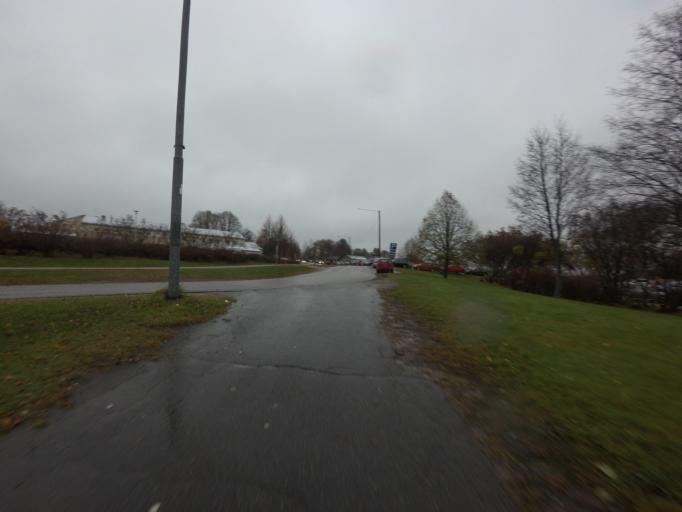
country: FI
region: Uusimaa
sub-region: Helsinki
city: Espoo
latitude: 60.2117
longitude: 24.6560
